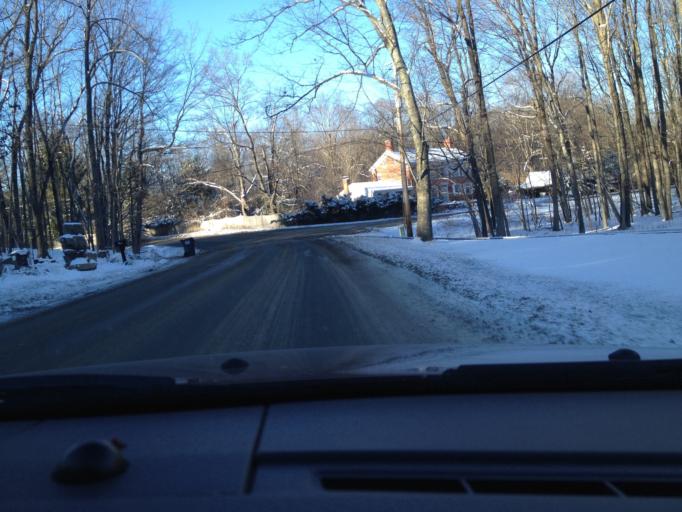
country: US
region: New York
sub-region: Rensselaer County
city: Averill Park
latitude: 42.6238
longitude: -73.5763
